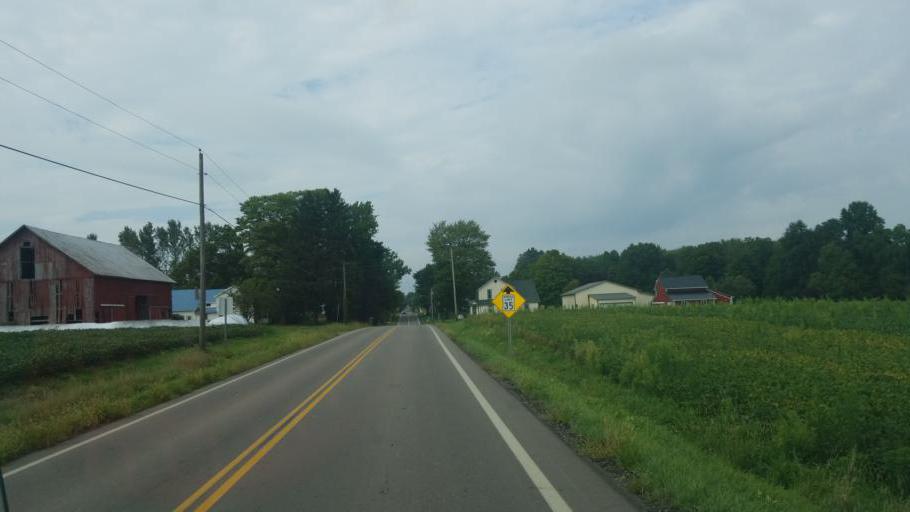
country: US
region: Ohio
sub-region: Wayne County
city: West Salem
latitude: 40.9201
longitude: -82.0519
